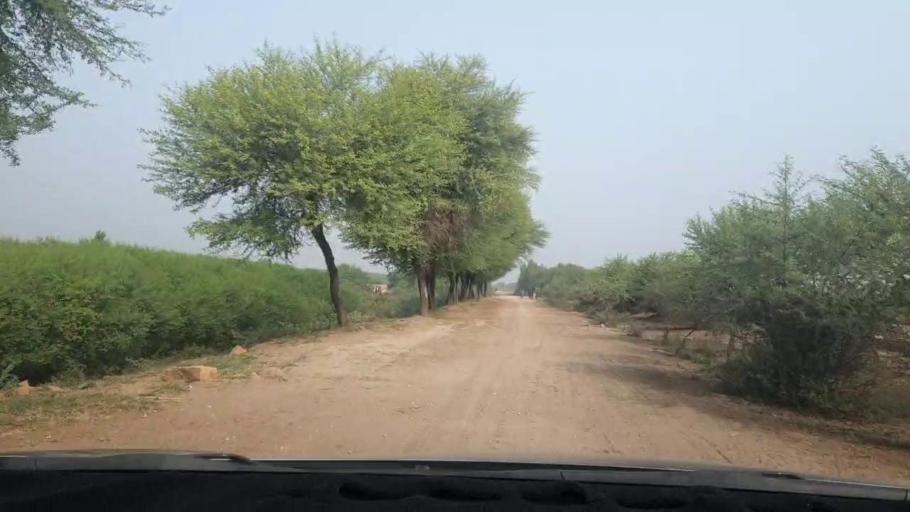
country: PK
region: Sindh
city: Matiari
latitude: 25.6474
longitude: 68.5607
